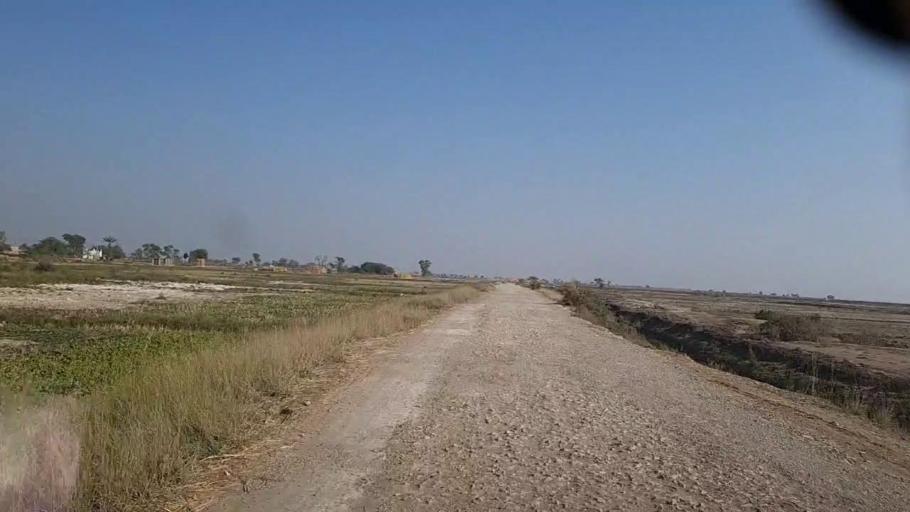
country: PK
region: Sindh
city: Jacobabad
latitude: 28.3062
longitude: 68.6048
